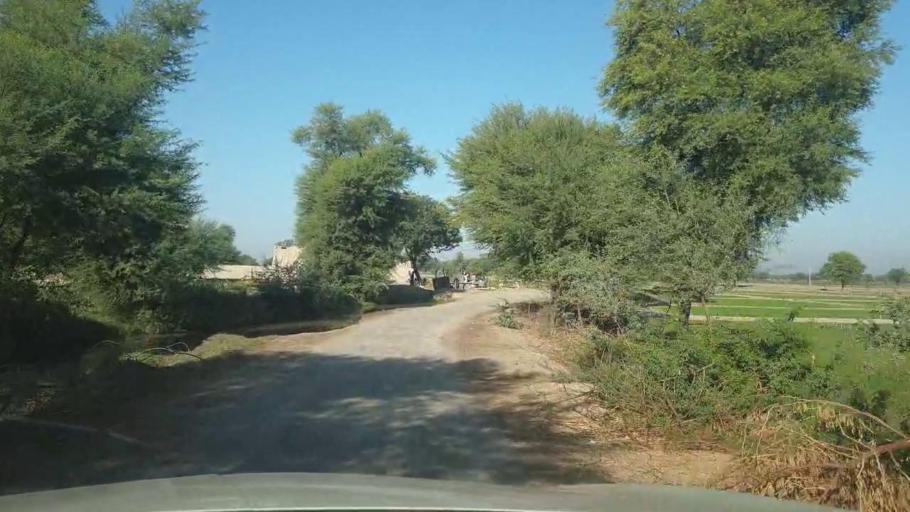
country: PK
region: Sindh
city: Bhan
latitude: 26.5466
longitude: 67.6713
